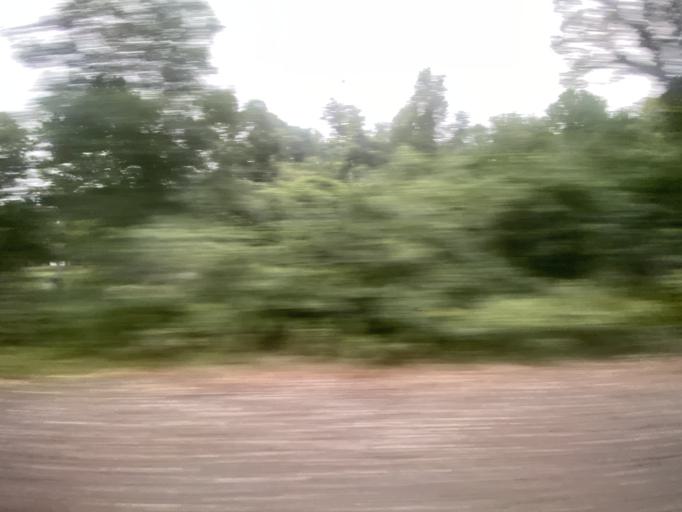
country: US
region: Indiana
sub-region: LaPorte County
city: Westville
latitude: 41.5995
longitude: -86.9009
